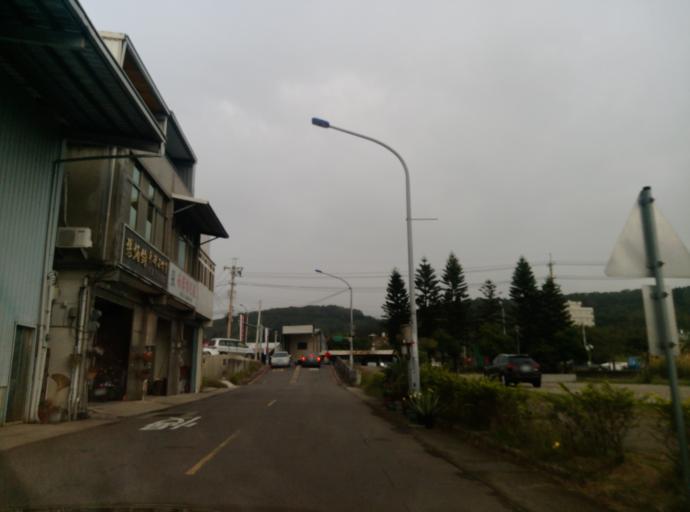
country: TW
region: Taiwan
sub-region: Hsinchu
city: Hsinchu
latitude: 24.7851
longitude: 120.9198
